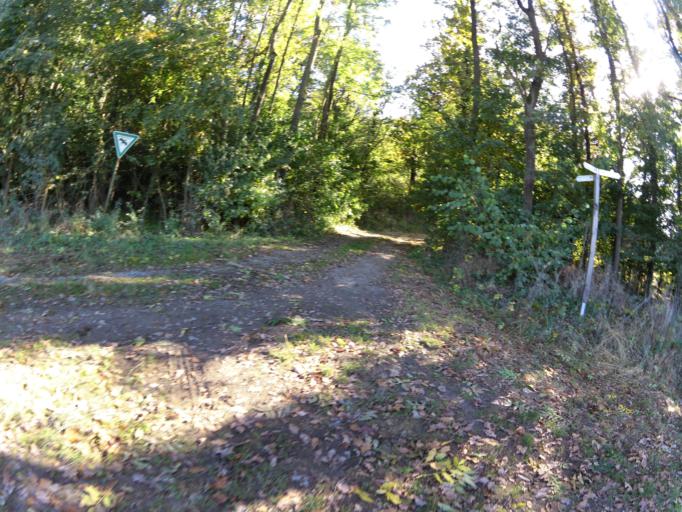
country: DE
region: Bavaria
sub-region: Regierungsbezirk Unterfranken
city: Ochsenfurt
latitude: 49.6908
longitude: 10.0644
